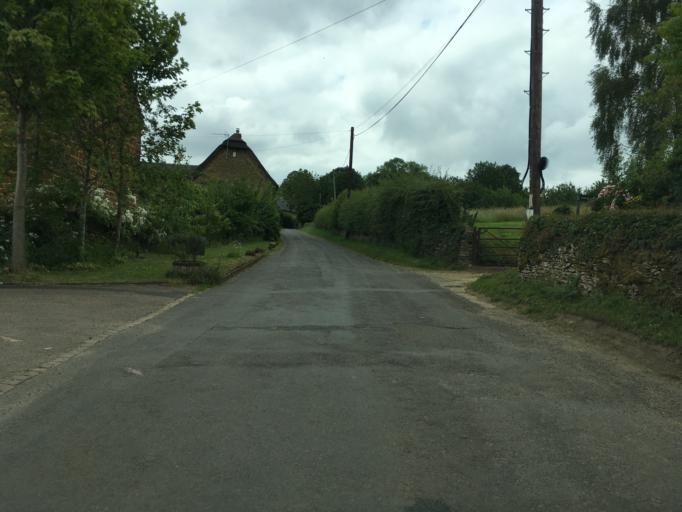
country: GB
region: England
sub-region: Oxfordshire
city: Hook Norton
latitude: 51.9534
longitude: -1.4425
